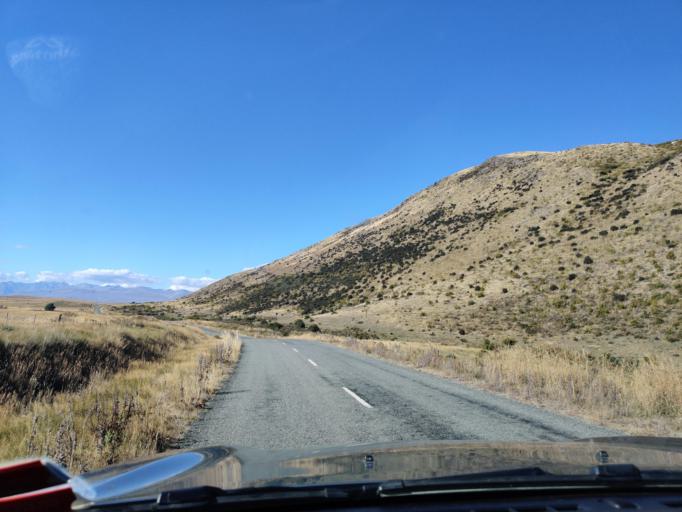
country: NZ
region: Canterbury
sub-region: Timaru District
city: Pleasant Point
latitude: -43.9883
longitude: 170.4537
